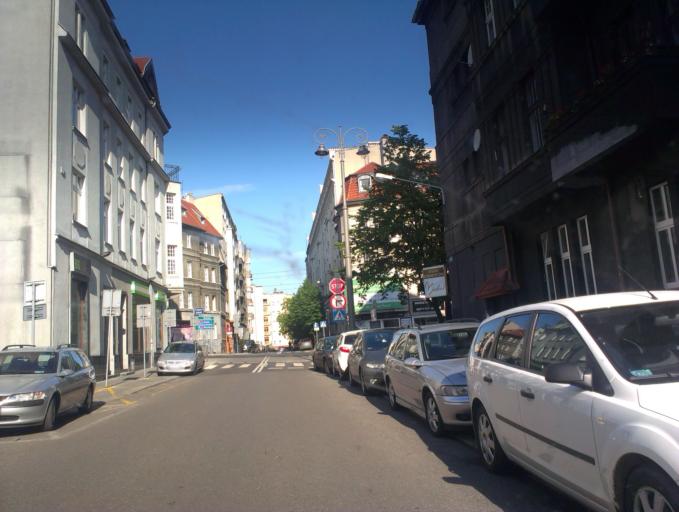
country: PL
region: Silesian Voivodeship
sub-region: Katowice
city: Katowice
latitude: 50.2516
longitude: 19.0154
